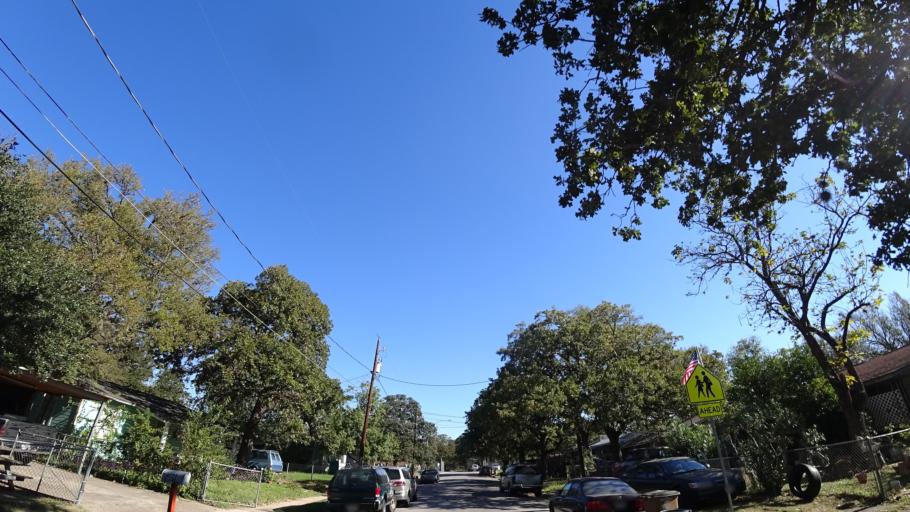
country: US
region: Texas
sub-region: Travis County
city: Austin
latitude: 30.2344
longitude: -97.6921
